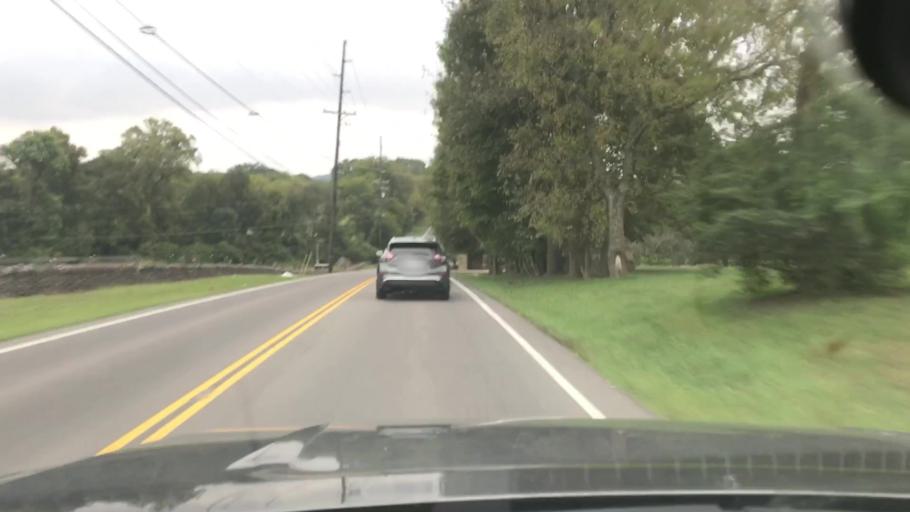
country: US
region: Tennessee
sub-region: Davidson County
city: Forest Hills
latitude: 36.0520
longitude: -86.8906
